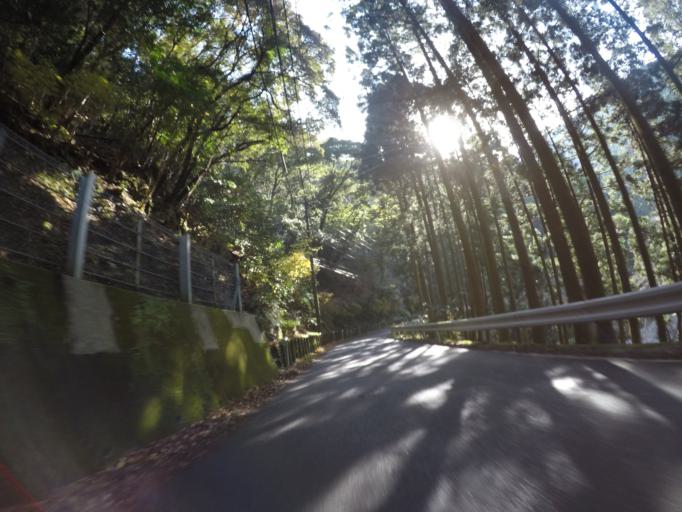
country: JP
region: Shizuoka
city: Heda
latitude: 34.8053
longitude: 138.8227
